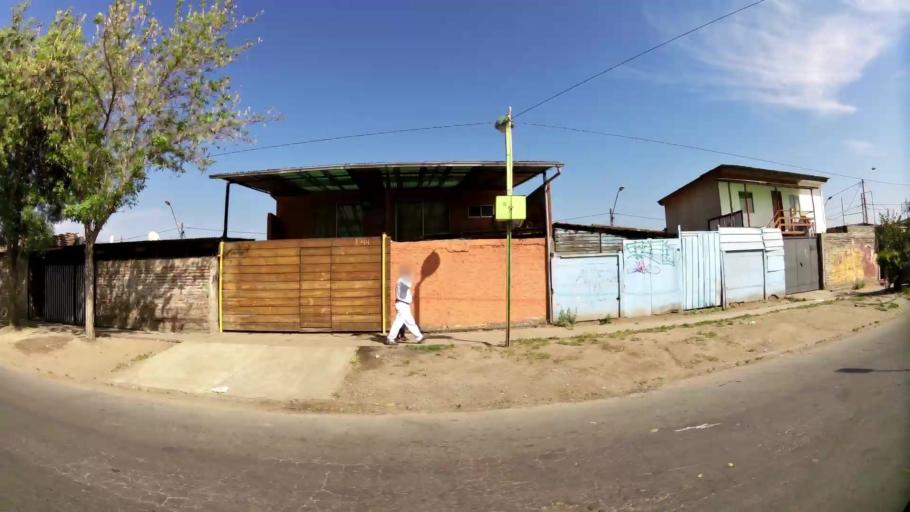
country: CL
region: Santiago Metropolitan
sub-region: Provincia de Santiago
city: Santiago
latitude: -33.3851
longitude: -70.6649
